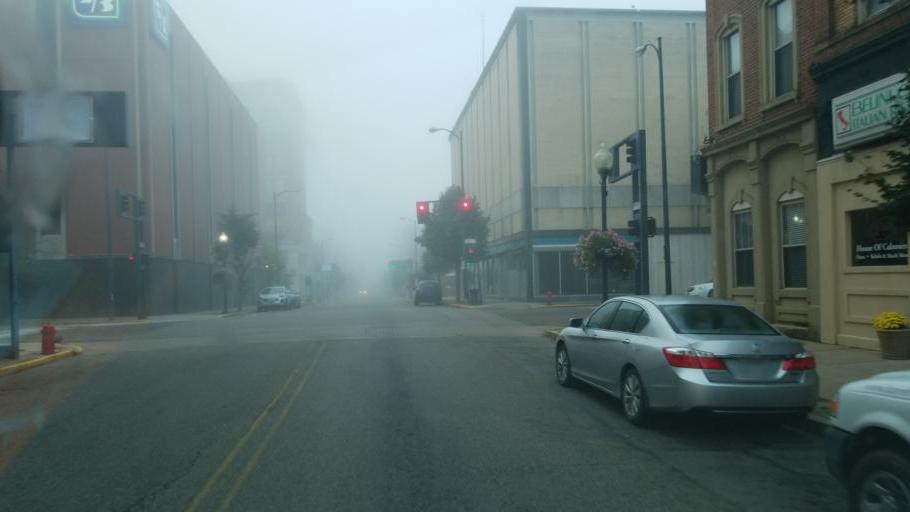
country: US
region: Ohio
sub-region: Scioto County
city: Portsmouth
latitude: 38.7351
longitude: -82.9965
